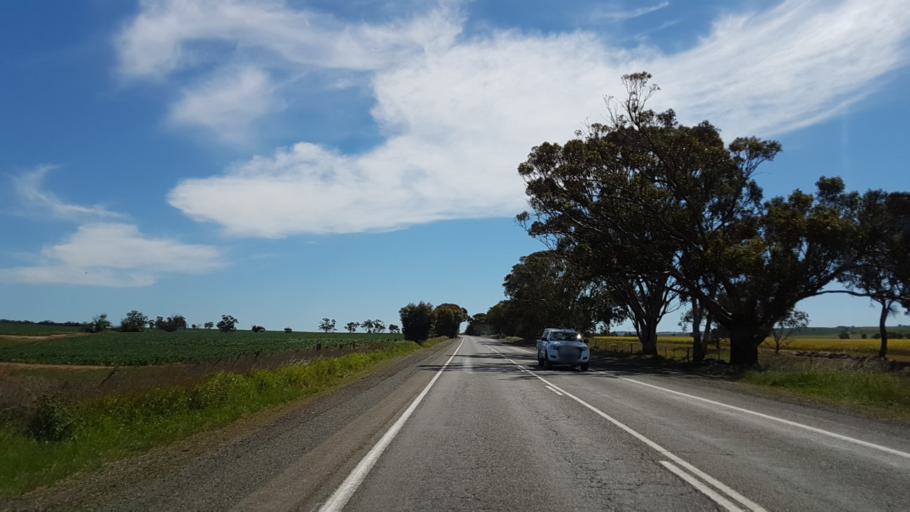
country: AU
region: South Australia
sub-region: Light
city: Freeling
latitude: -34.3340
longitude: 138.7870
